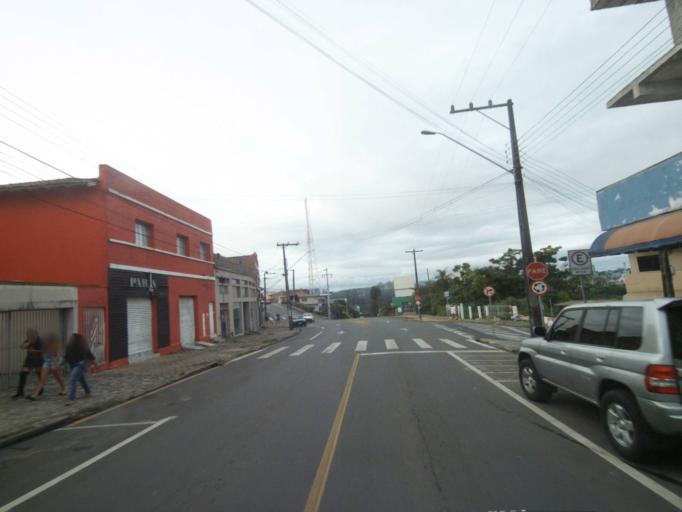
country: BR
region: Parana
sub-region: Telemaco Borba
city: Telemaco Borba
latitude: -24.3198
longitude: -50.6180
